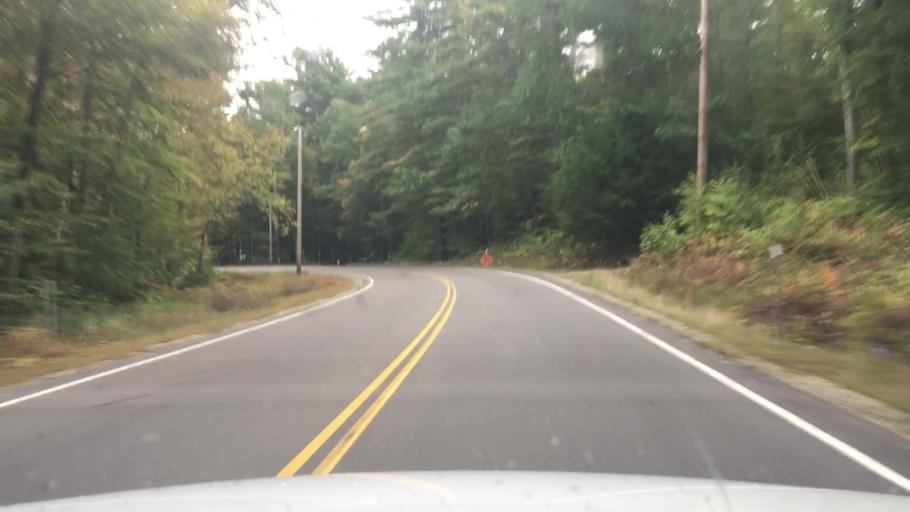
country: US
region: New Hampshire
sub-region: Carroll County
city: Wolfeboro
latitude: 43.5384
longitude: -71.2977
